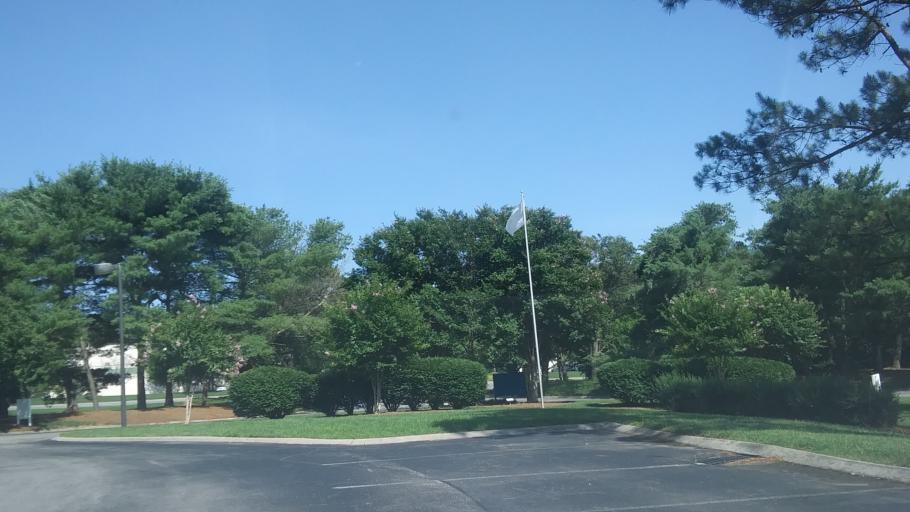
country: US
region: Tennessee
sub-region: Davidson County
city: Oak Hill
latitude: 36.0971
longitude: -86.6785
